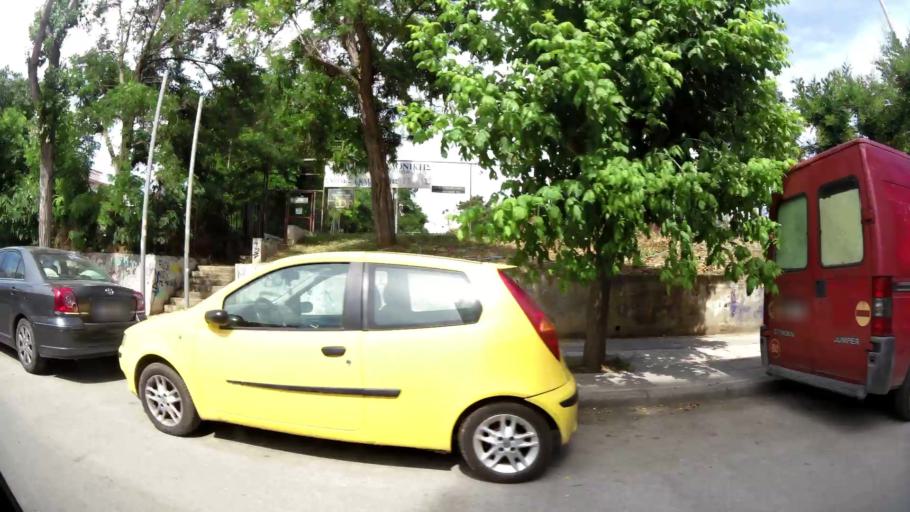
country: GR
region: Central Macedonia
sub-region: Nomos Thessalonikis
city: Kalamaria
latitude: 40.6020
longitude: 22.9592
